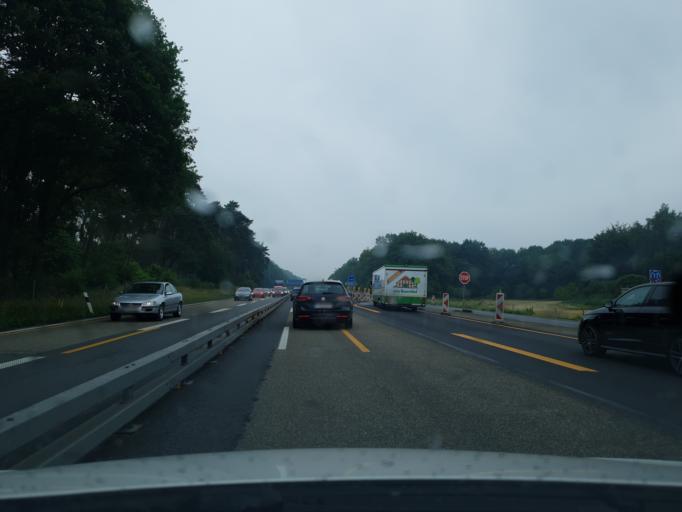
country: DE
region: North Rhine-Westphalia
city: Dorsten
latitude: 51.6969
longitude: 6.9245
